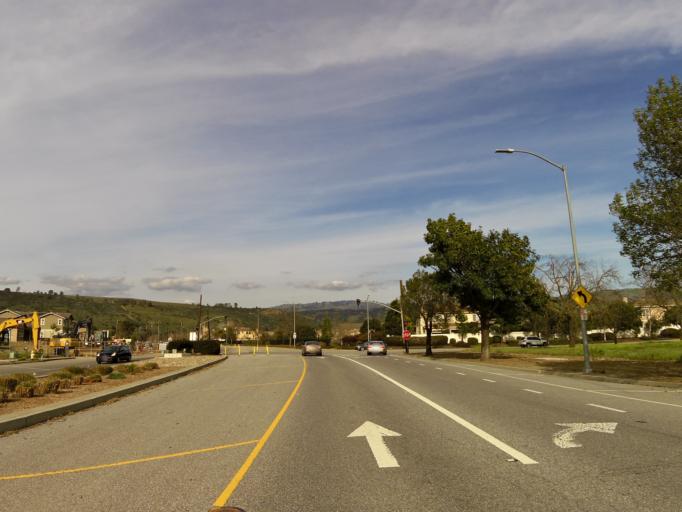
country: US
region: California
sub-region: Santa Clara County
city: Morgan Hill
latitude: 37.1560
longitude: -121.6479
